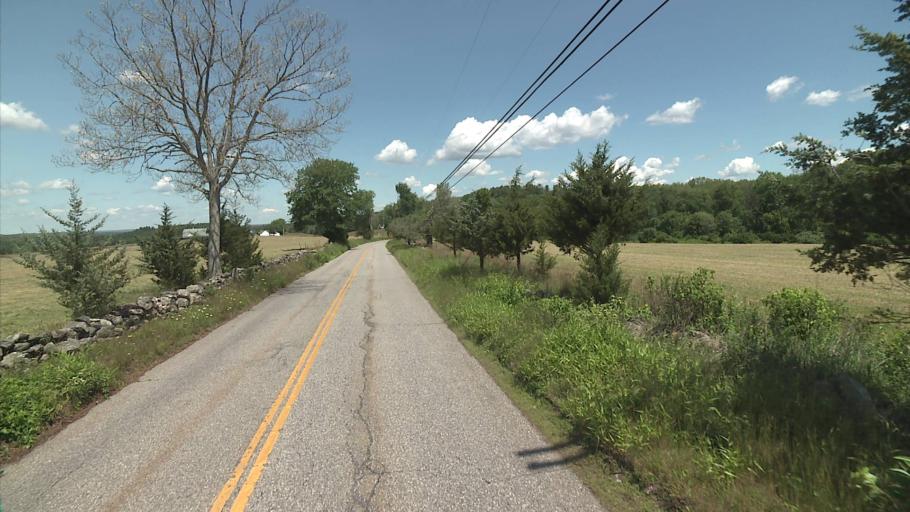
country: US
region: Connecticut
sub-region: New London County
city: Preston City
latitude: 41.5360
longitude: -71.8805
